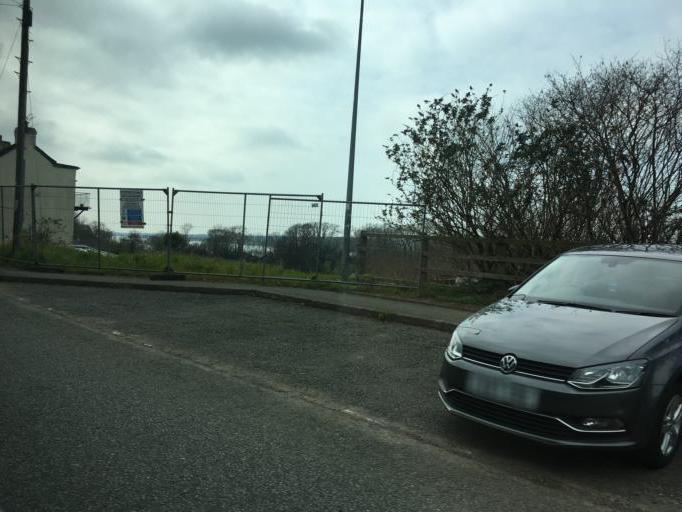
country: GB
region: Wales
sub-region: Gwynedd
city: Y Felinheli
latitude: 53.1806
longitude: -4.2138
